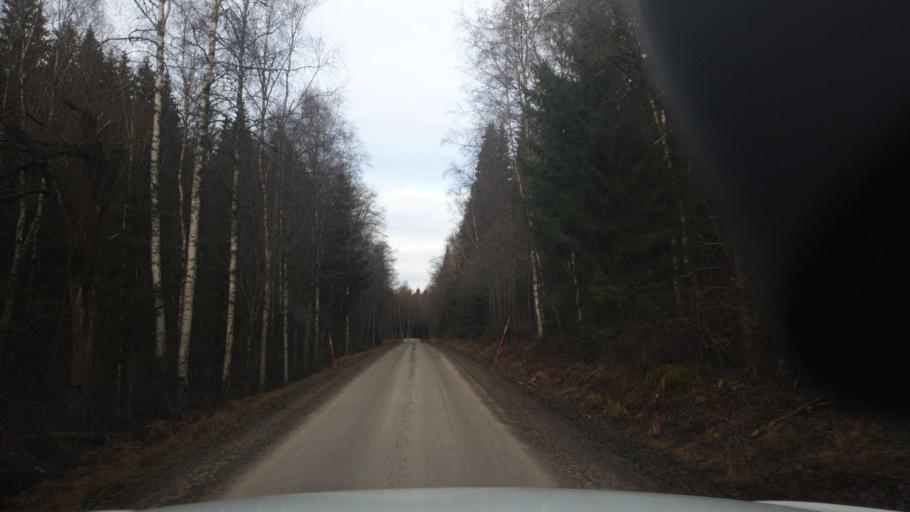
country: NO
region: Hedmark
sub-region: Eidskog
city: Skotterud
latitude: 59.8949
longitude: 11.9864
